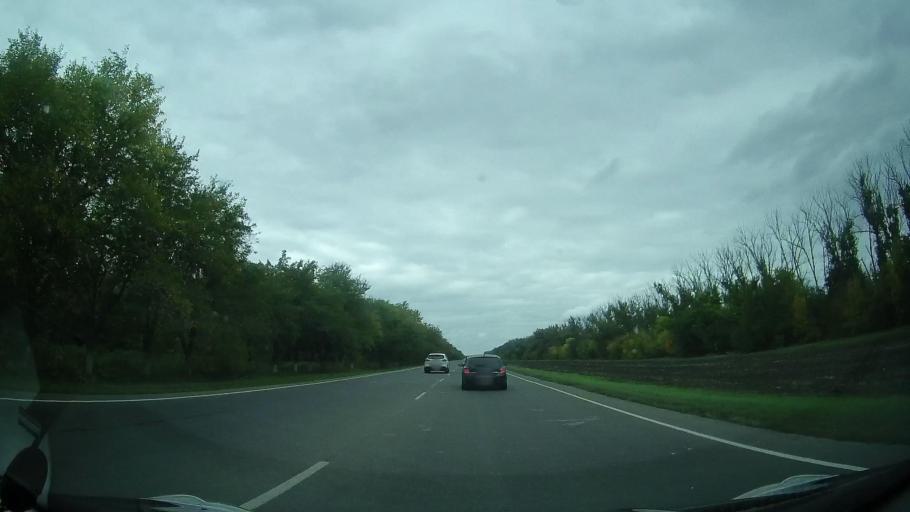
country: RU
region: Rostov
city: Yegorlykskaya
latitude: 46.6048
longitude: 40.6138
